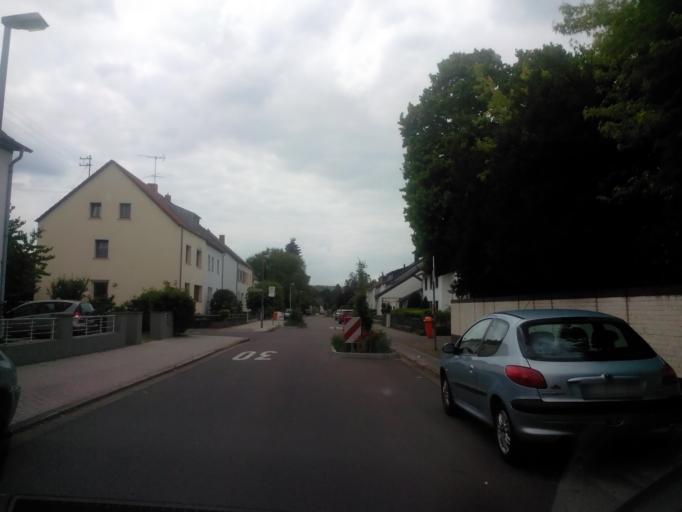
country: DE
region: Saarland
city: Saarlouis
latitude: 49.3125
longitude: 6.7416
